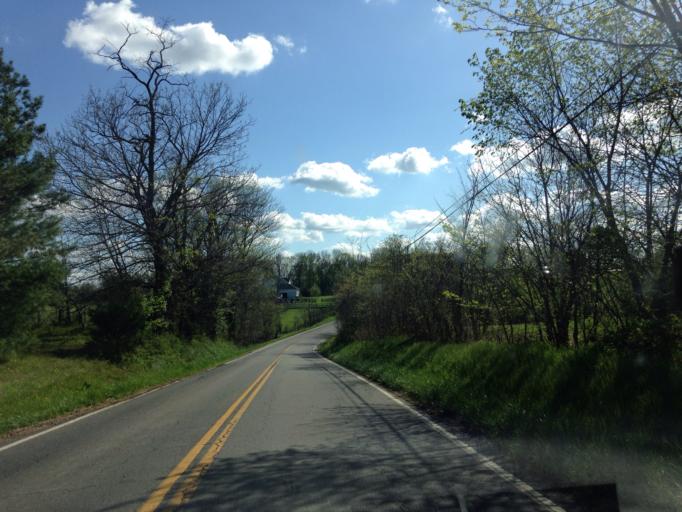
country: US
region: Virginia
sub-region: Loudoun County
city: Lovettsville
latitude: 39.2741
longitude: -77.5950
